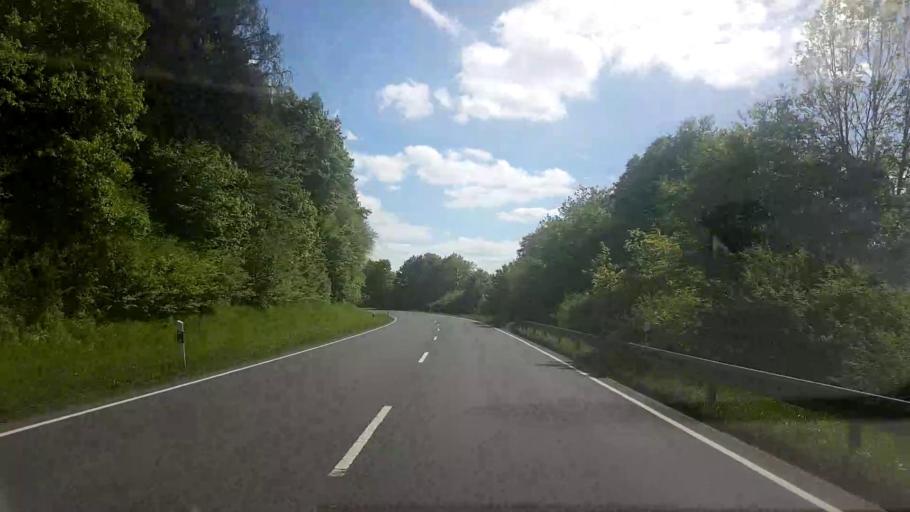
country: DE
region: Bavaria
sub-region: Upper Franconia
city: Rattelsdorf
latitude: 50.0553
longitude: 10.8781
